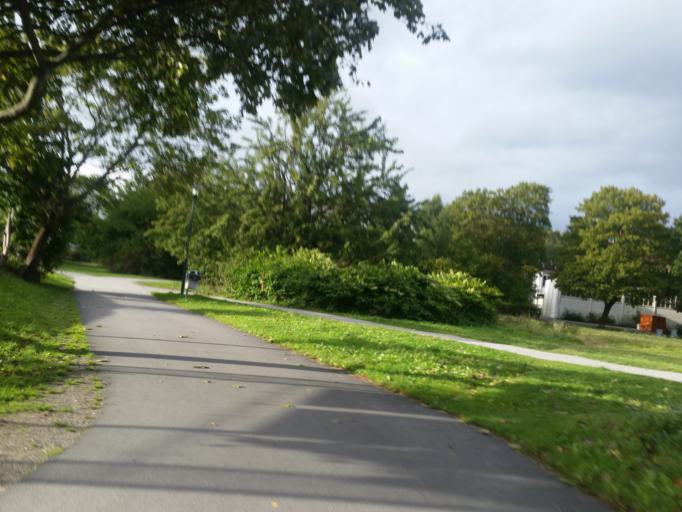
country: SE
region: Stockholm
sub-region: Stockholms Kommun
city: Arsta
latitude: 59.2895
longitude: 18.1009
